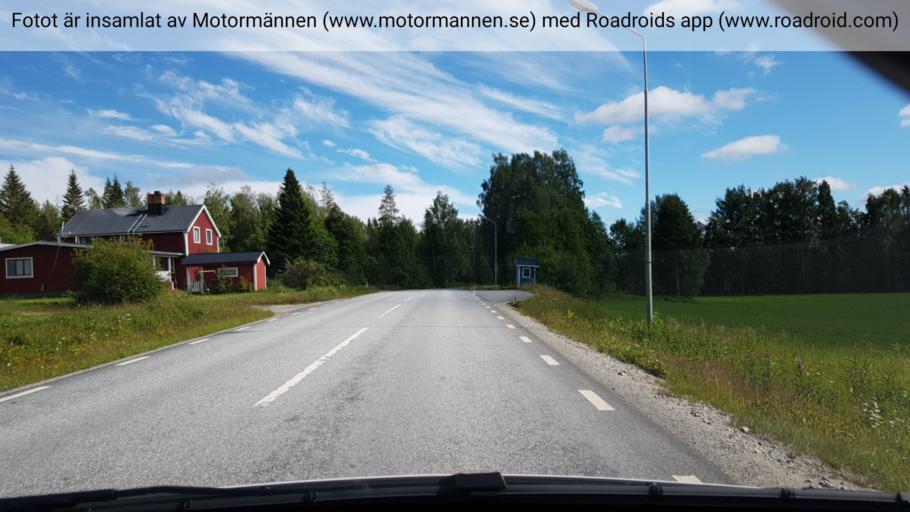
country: SE
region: Vaesterbotten
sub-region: Vindelns Kommun
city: Vindeln
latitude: 64.1116
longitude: 19.5833
